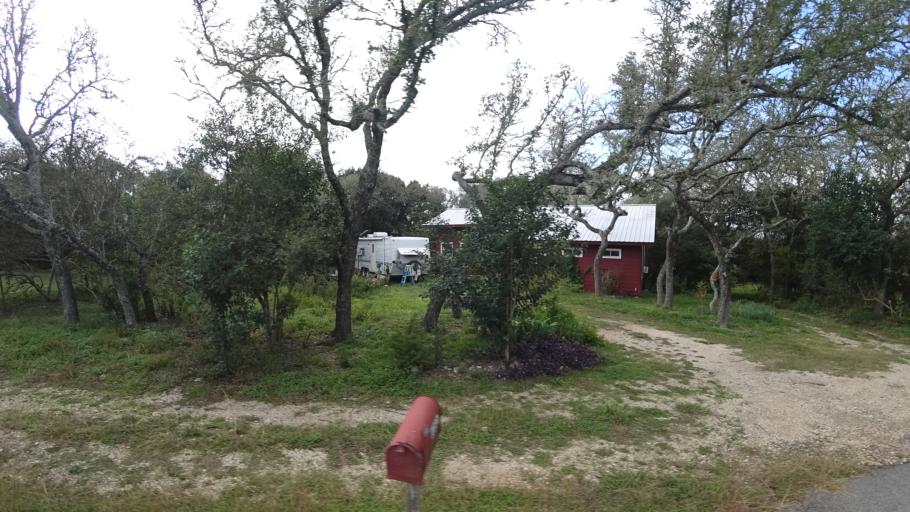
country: US
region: Texas
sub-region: Travis County
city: Bee Cave
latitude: 30.2542
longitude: -97.9240
